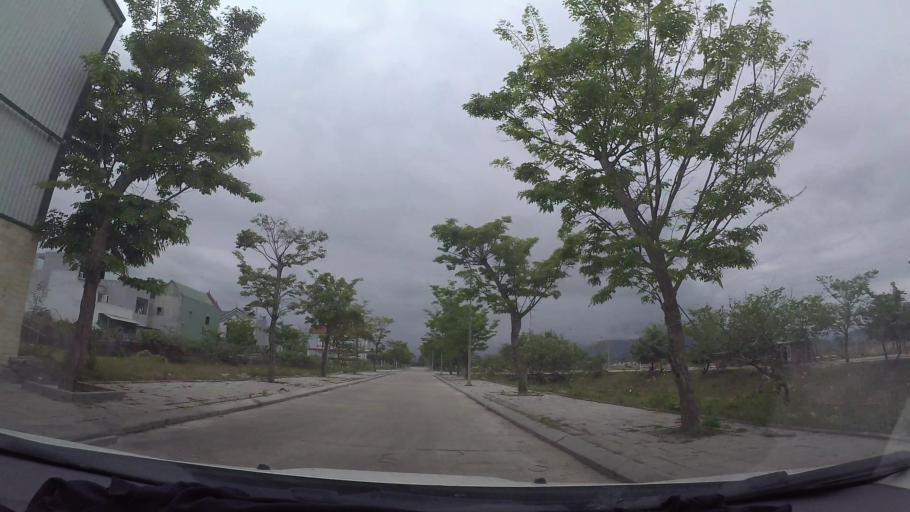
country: VN
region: Da Nang
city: Lien Chieu
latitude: 16.1039
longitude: 108.1161
